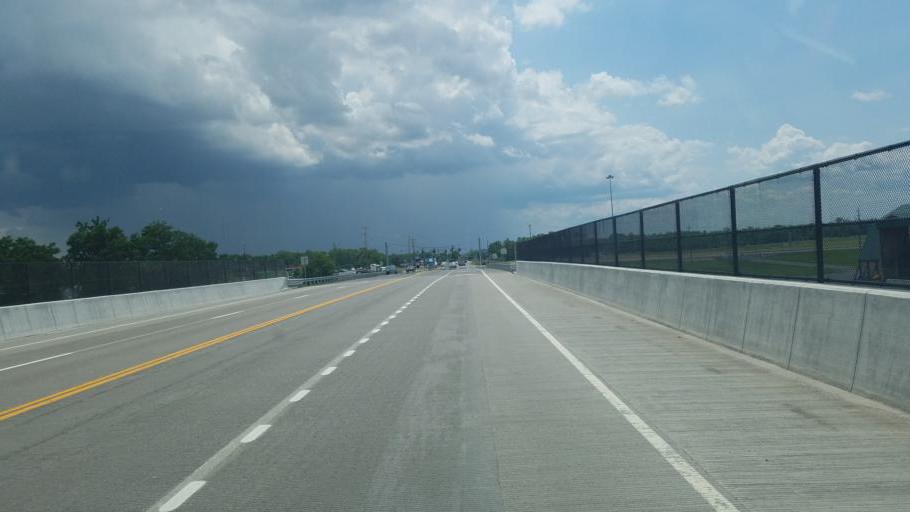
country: US
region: New York
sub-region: Seneca County
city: Waterloo
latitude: 42.9681
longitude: -76.8474
